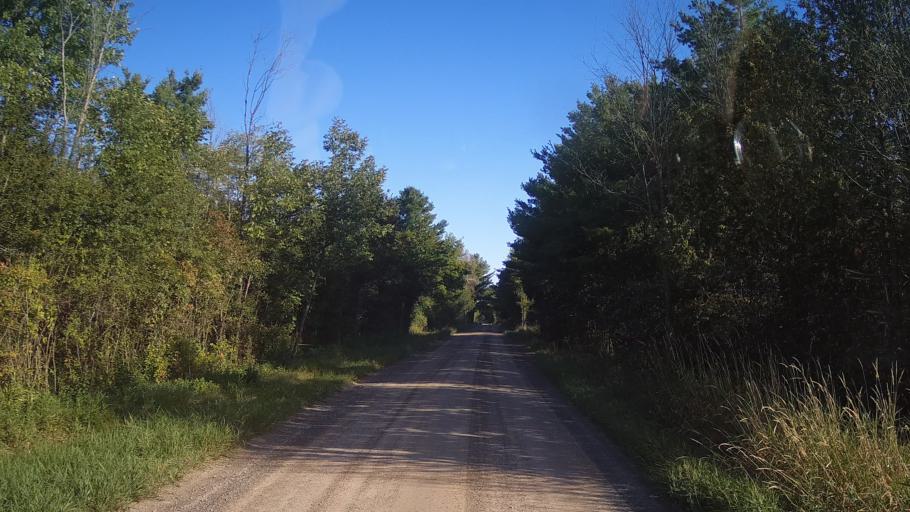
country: US
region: New York
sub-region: Jefferson County
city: Alexandria Bay
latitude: 44.4101
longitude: -75.9763
